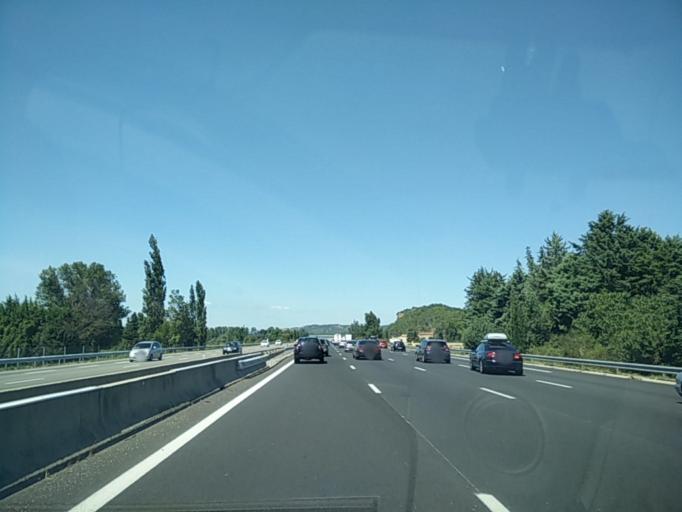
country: FR
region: Provence-Alpes-Cote d'Azur
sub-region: Departement du Vaucluse
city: Piolenc
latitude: 44.1603
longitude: 4.7685
